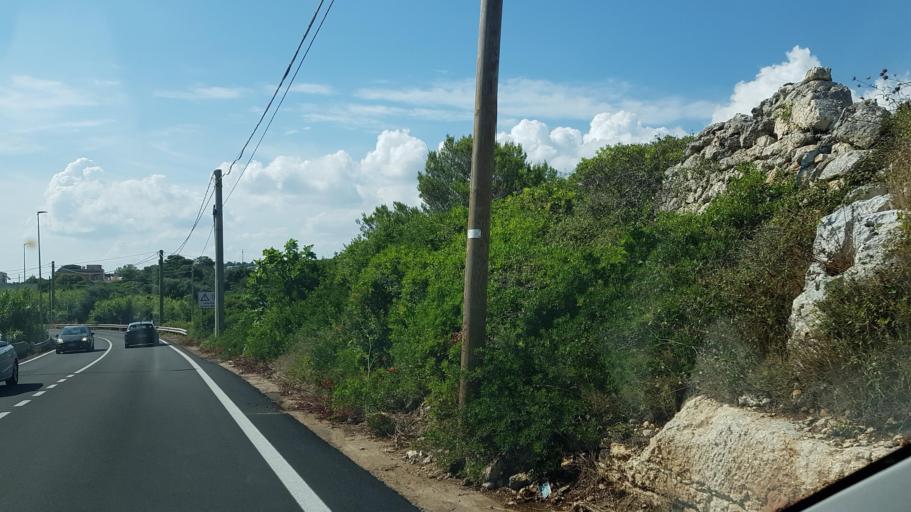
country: IT
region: Apulia
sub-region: Provincia di Lecce
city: Leuca
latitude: 39.8088
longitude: 18.3260
